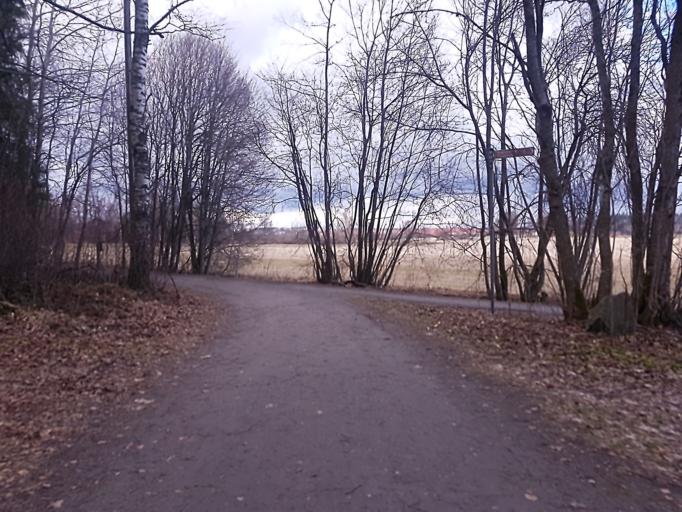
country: FI
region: Uusimaa
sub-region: Helsinki
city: Helsinki
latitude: 60.2721
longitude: 24.9376
